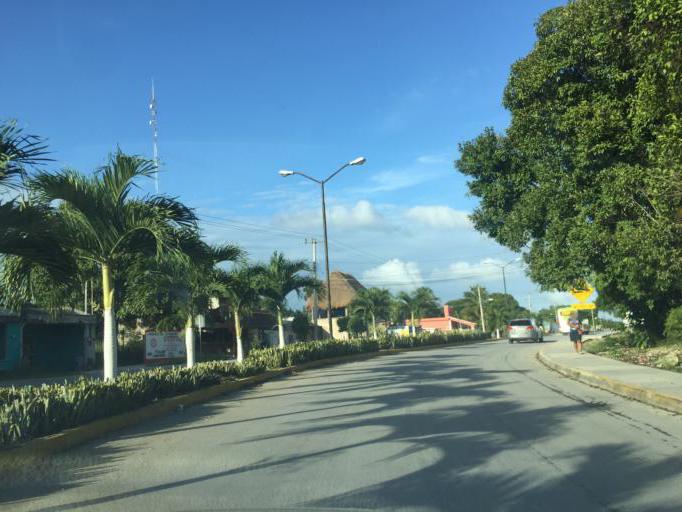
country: MX
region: Quintana Roo
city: Coba
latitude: 20.4937
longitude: -87.7362
